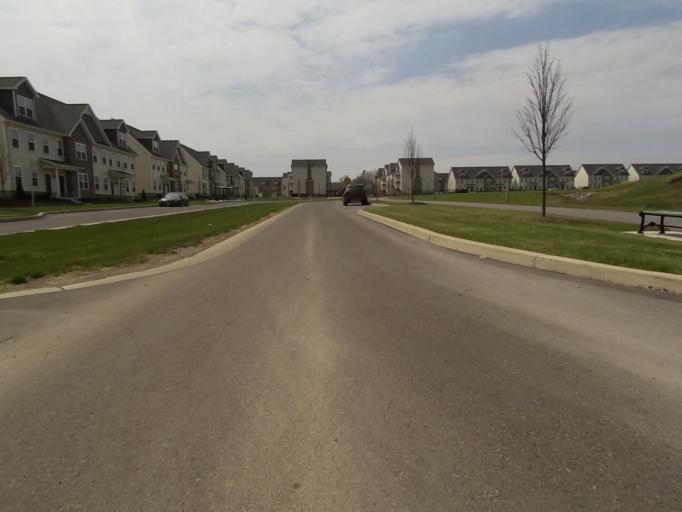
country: US
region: Pennsylvania
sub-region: Centre County
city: Park Forest Village
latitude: 40.7894
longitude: -77.8941
